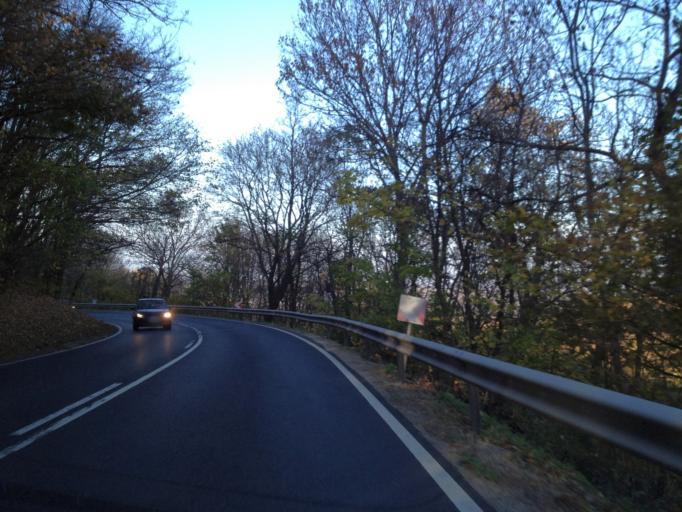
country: HU
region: Veszprem
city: Zirc
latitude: 47.3393
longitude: 17.8850
